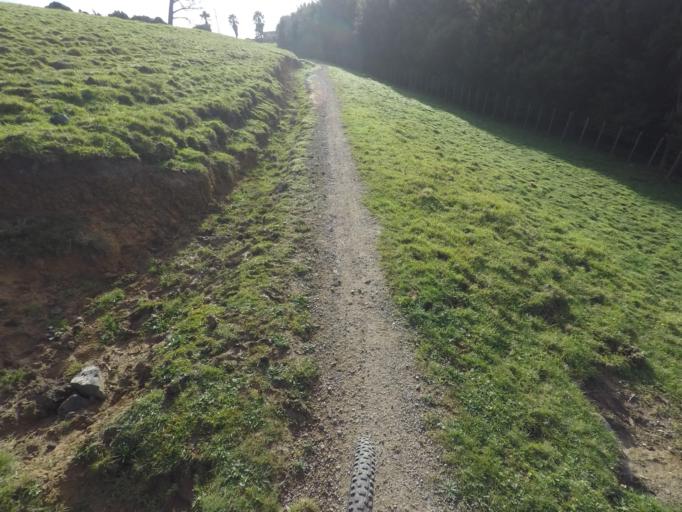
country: NZ
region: Auckland
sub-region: Auckland
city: Manukau City
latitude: -36.9900
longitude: 174.9121
